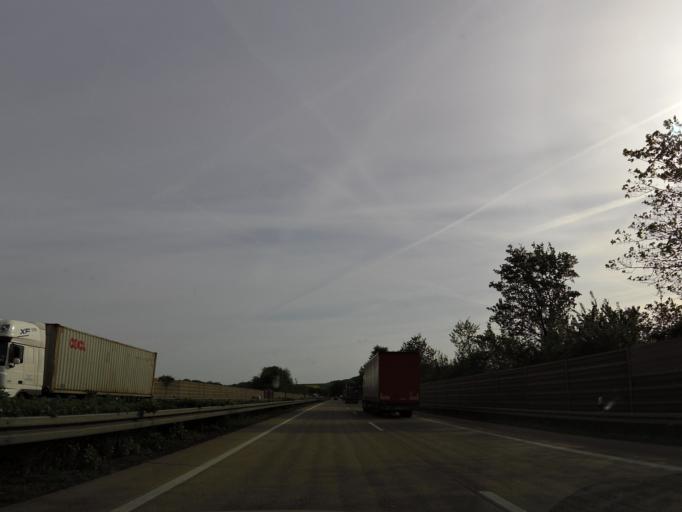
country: DE
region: Lower Saxony
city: Kalefeld
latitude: 51.8093
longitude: 10.0964
